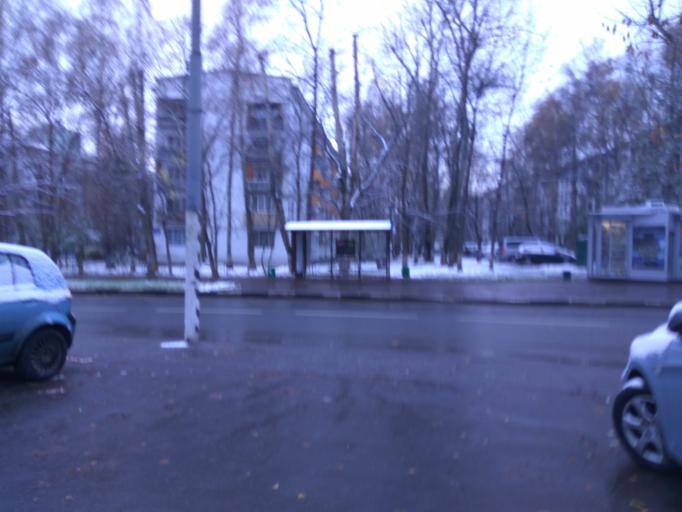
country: RU
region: Moscow
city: Orekhovo-Borisovo Severnoye
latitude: 55.6297
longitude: 37.6728
